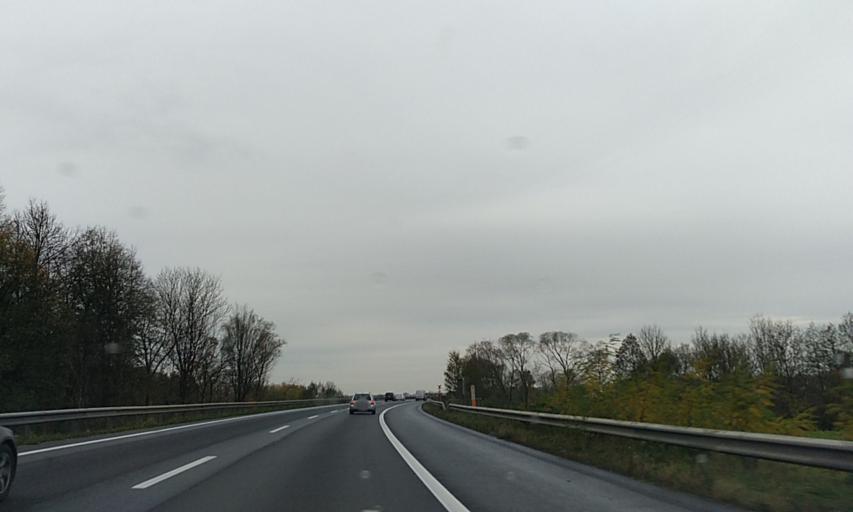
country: AT
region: Upper Austria
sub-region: Politischer Bezirk Linz-Land
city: Traun
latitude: 48.1926
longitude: 14.2310
